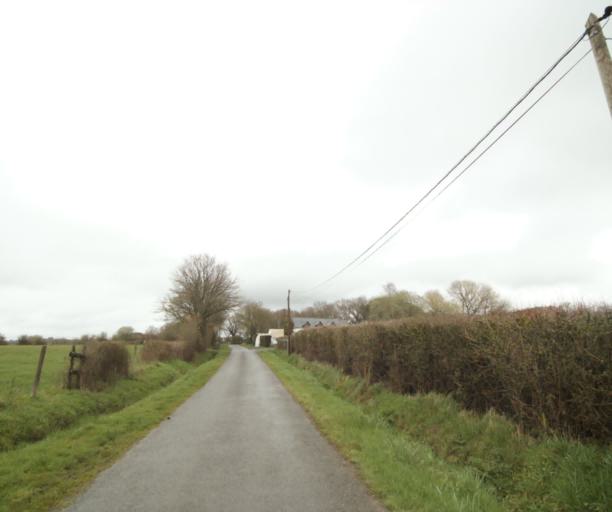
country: FR
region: Pays de la Loire
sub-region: Departement de la Loire-Atlantique
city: Quilly
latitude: 47.4552
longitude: -1.9009
